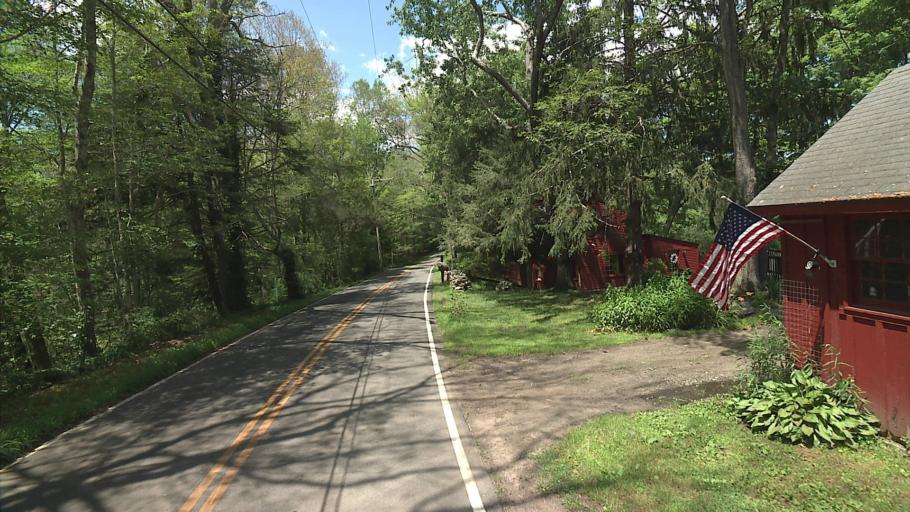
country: US
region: Connecticut
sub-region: Middlesex County
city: Essex Village
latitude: 41.4473
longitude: -72.3380
